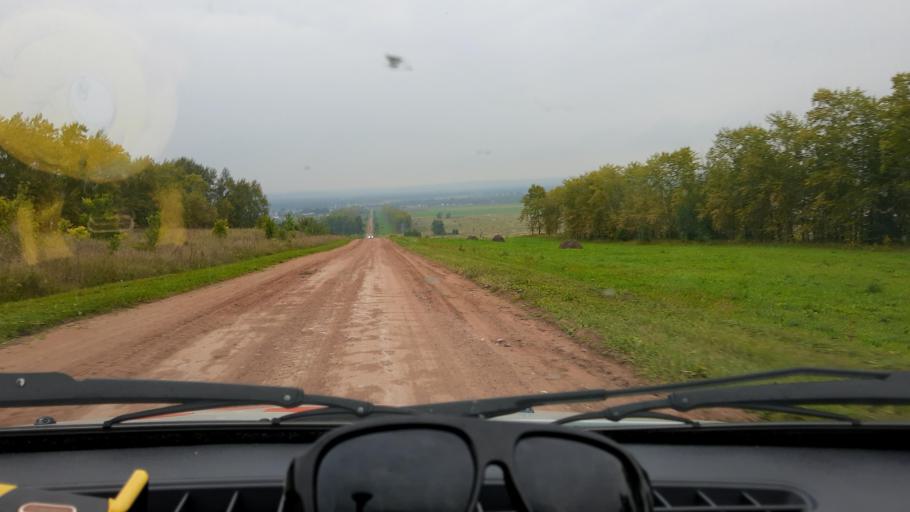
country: RU
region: Bashkortostan
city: Asanovo
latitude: 54.9972
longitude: 55.7025
